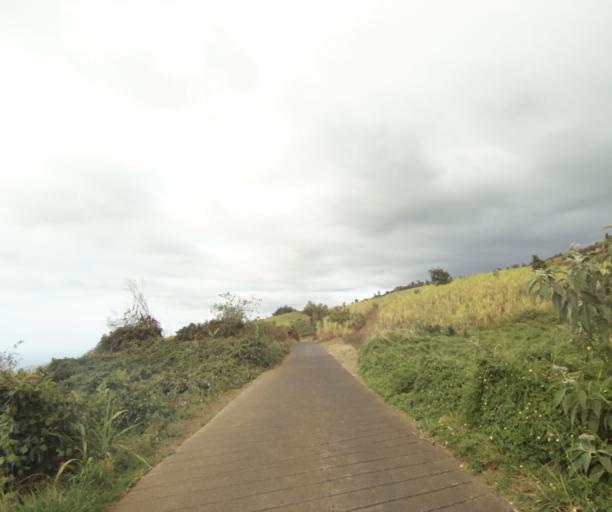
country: RE
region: Reunion
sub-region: Reunion
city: Saint-Paul
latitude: -21.0289
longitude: 55.3175
